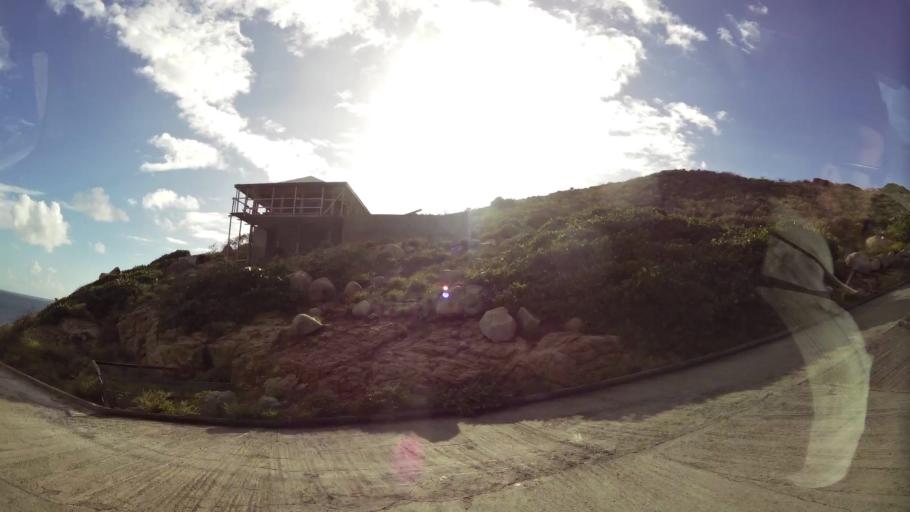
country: VG
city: Tortola
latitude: 18.4327
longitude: -64.4246
